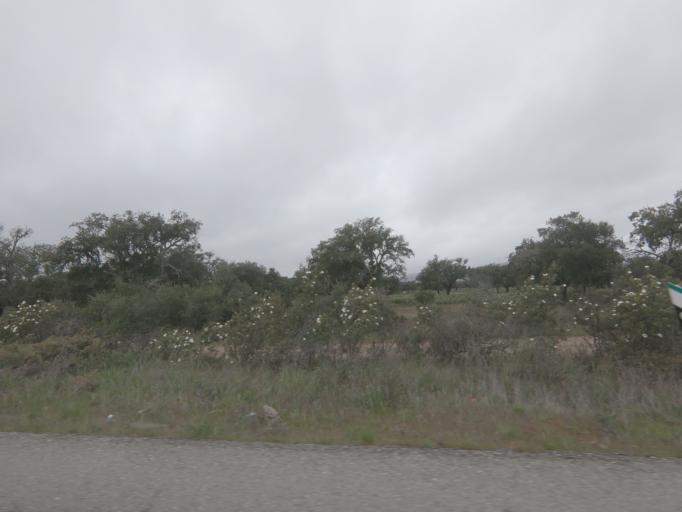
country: ES
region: Extremadura
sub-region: Provincia de Caceres
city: Malpartida de Caceres
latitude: 39.3075
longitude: -6.5149
